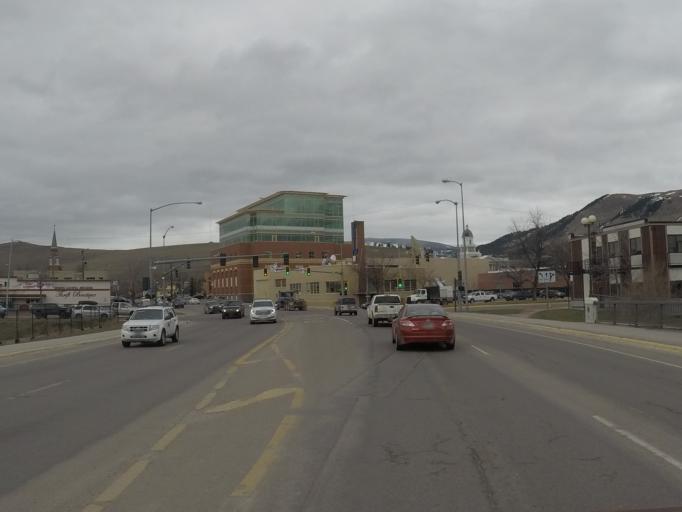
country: US
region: Montana
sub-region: Missoula County
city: Missoula
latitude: 46.8720
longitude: -113.9997
